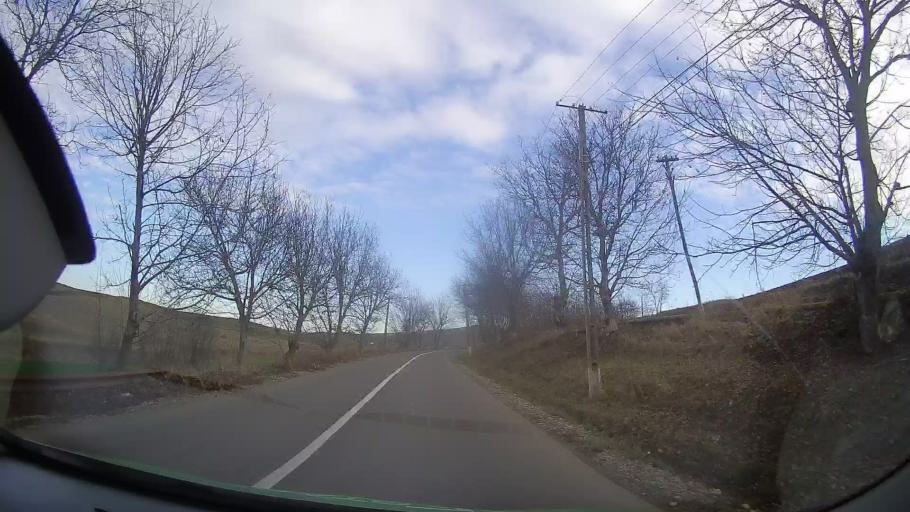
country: RO
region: Mures
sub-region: Comuna Iclanzel
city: Iclanzel
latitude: 46.5067
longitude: 24.2591
